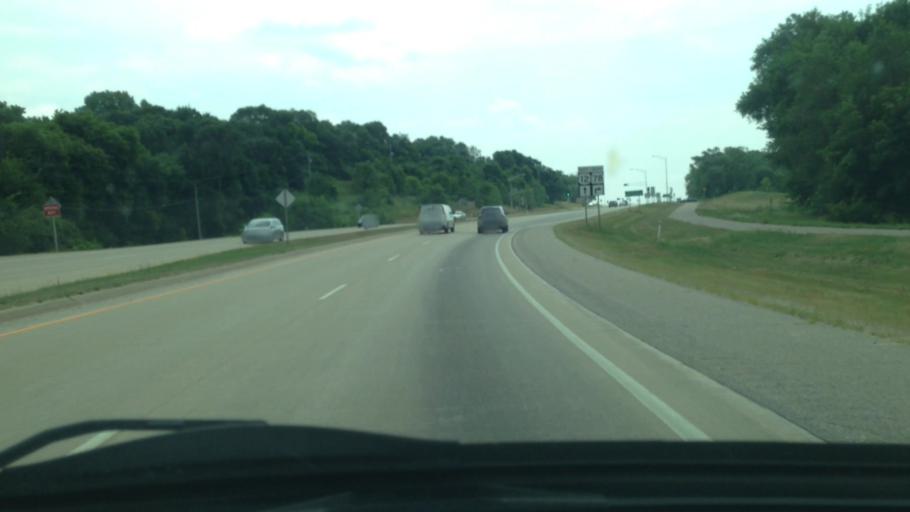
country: US
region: Wisconsin
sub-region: Sauk County
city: Sauk City
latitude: 43.2683
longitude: -89.7162
